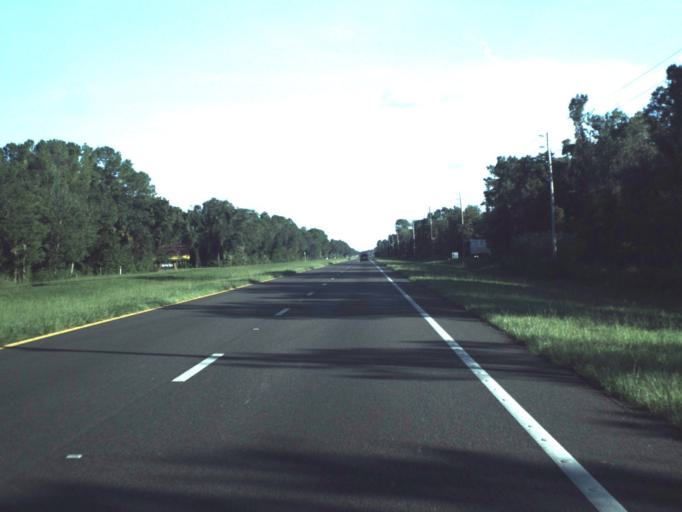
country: US
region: Florida
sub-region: Citrus County
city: Crystal River
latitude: 28.9394
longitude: -82.6204
